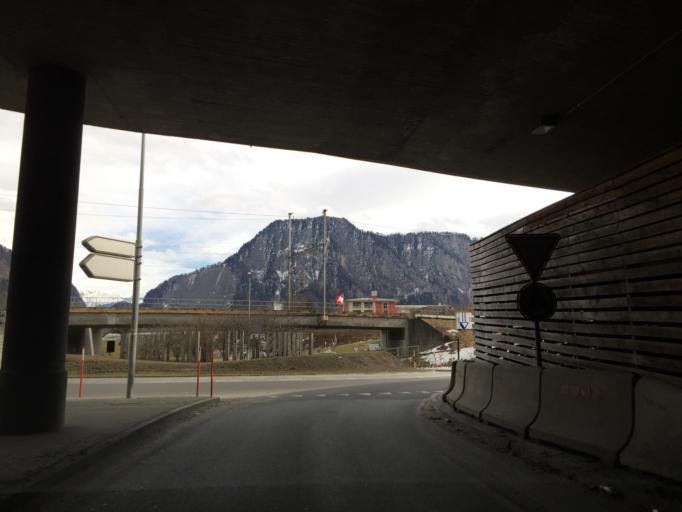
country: CH
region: Grisons
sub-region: Landquart District
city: Malans
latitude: 46.9715
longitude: 9.5521
